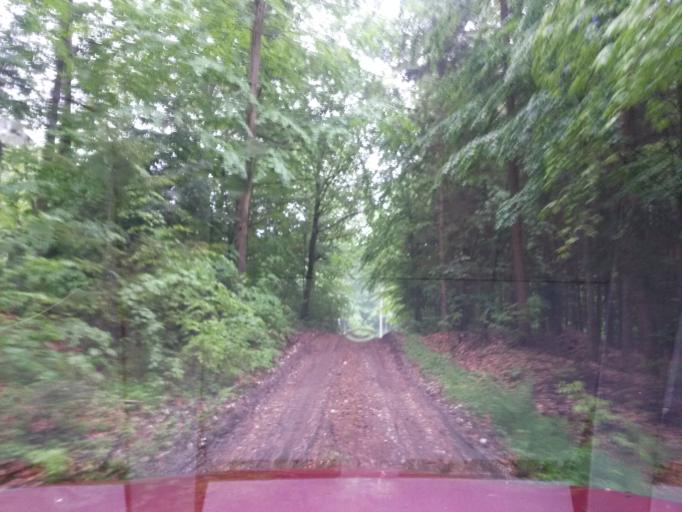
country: SK
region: Kosicky
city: Medzev
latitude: 48.7881
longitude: 20.7874
